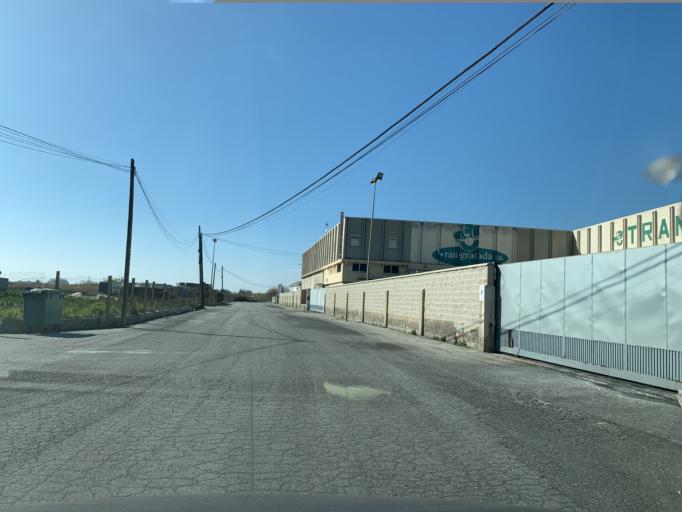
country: ES
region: Andalusia
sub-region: Provincia de Granada
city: El Varadero
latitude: 36.7271
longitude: -3.5422
